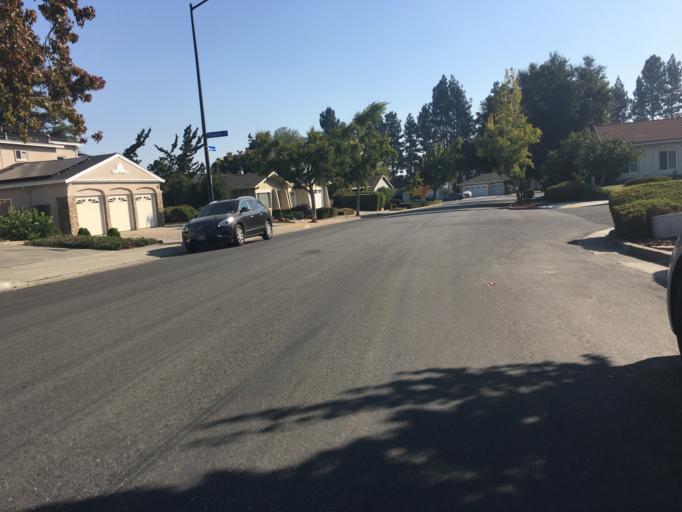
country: US
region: California
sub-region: Santa Clara County
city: Cupertino
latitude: 37.3317
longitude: -122.0477
